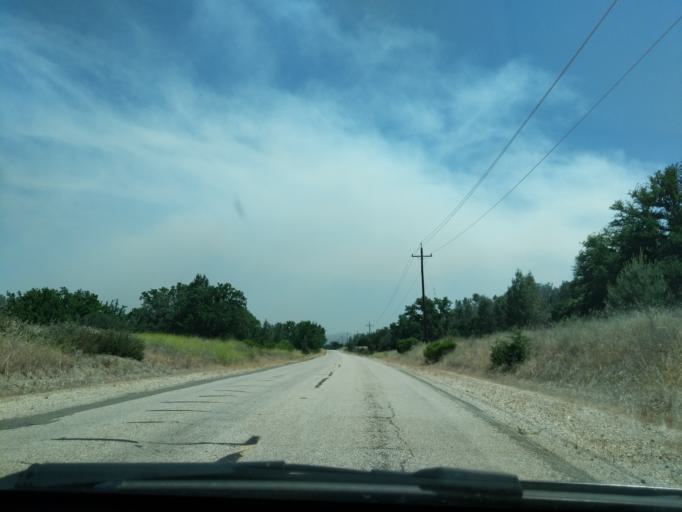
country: US
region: California
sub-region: Monterey County
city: King City
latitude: 35.9819
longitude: -121.1778
